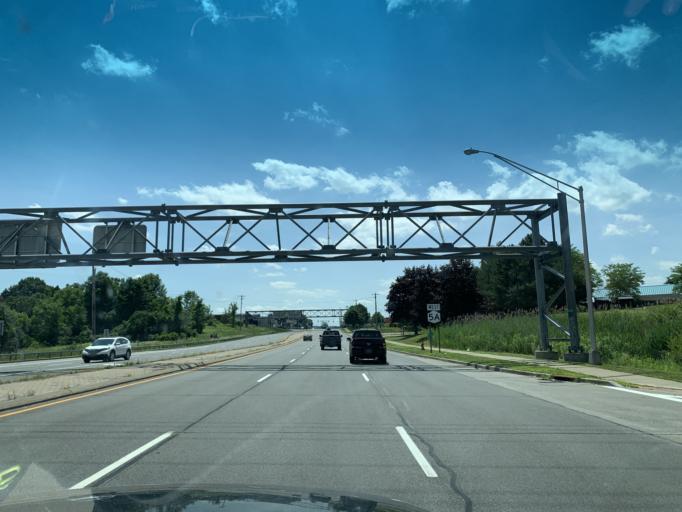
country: US
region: New York
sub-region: Oneida County
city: New York Mills
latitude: 43.0913
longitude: -75.3093
